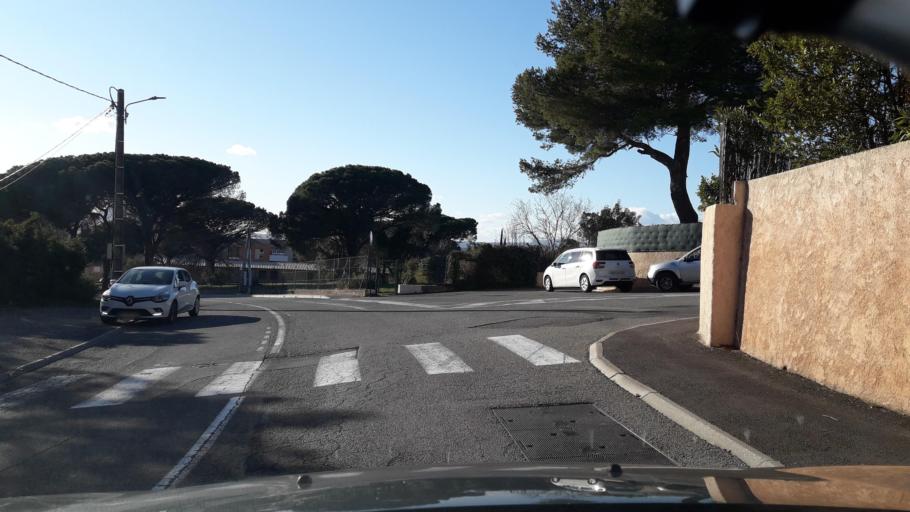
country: FR
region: Provence-Alpes-Cote d'Azur
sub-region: Departement du Var
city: Frejus
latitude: 43.4583
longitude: 6.7249
